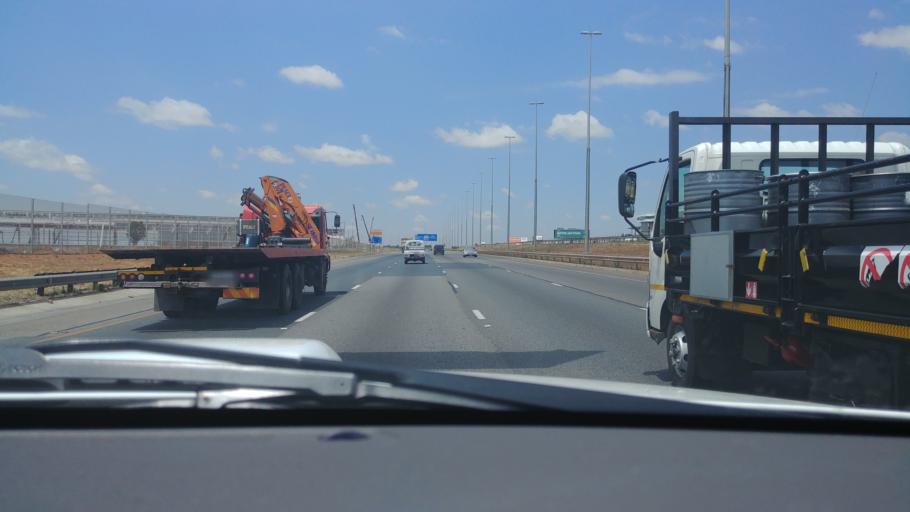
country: ZA
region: Gauteng
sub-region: Ekurhuleni Metropolitan Municipality
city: Tembisa
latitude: -26.0203
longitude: 28.2606
